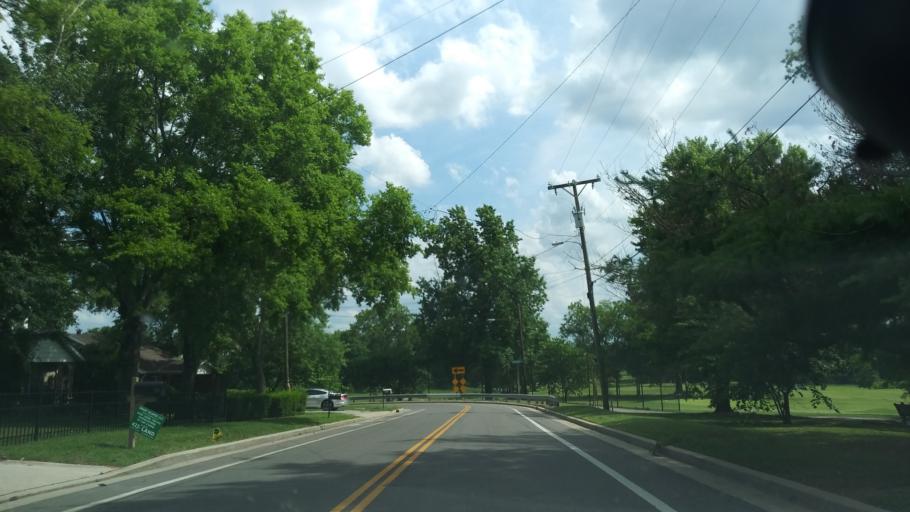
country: US
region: Tennessee
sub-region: Davidson County
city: Belle Meade
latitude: 36.1437
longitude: -86.8482
